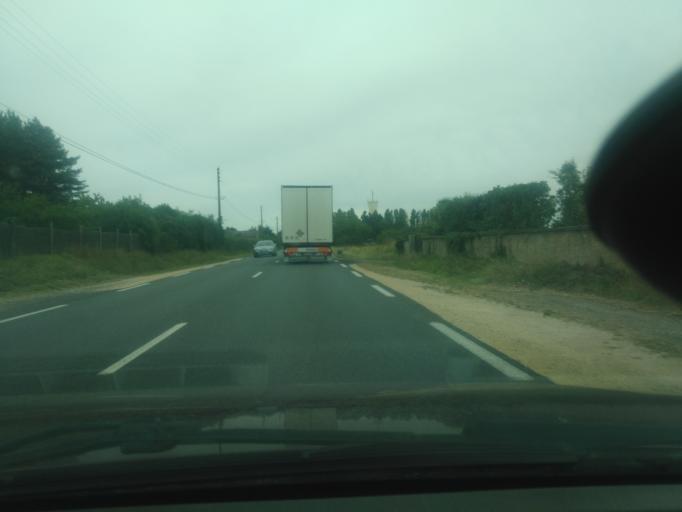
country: FR
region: Poitou-Charentes
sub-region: Departement de la Vienne
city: Sevres-Anxaumont
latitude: 46.5596
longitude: 0.4538
